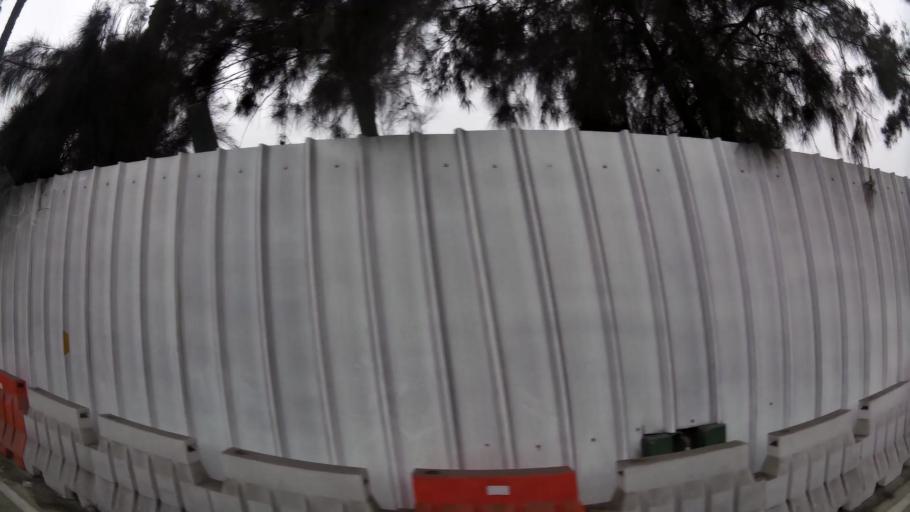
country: PE
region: Lima
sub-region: Lima
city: San Luis
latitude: -12.0975
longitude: -76.9797
